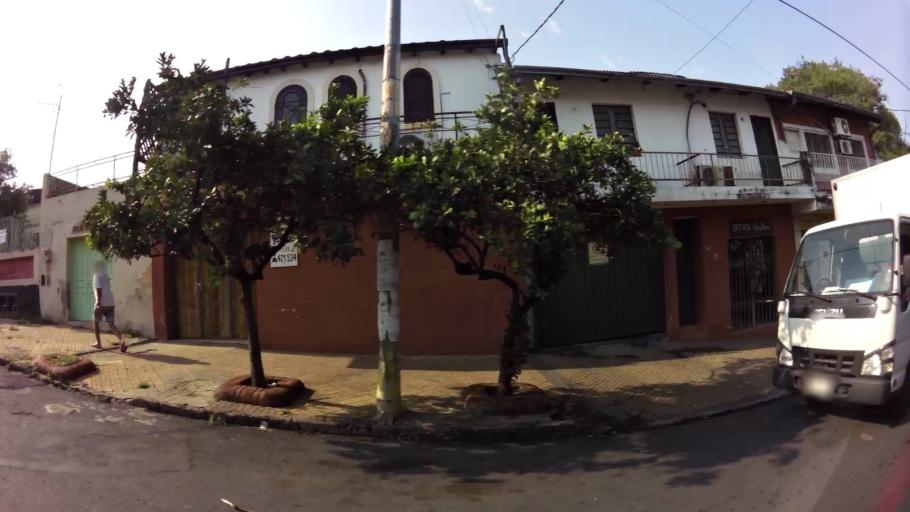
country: PY
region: Presidente Hayes
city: Nanawa
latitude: -25.2804
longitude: -57.6564
